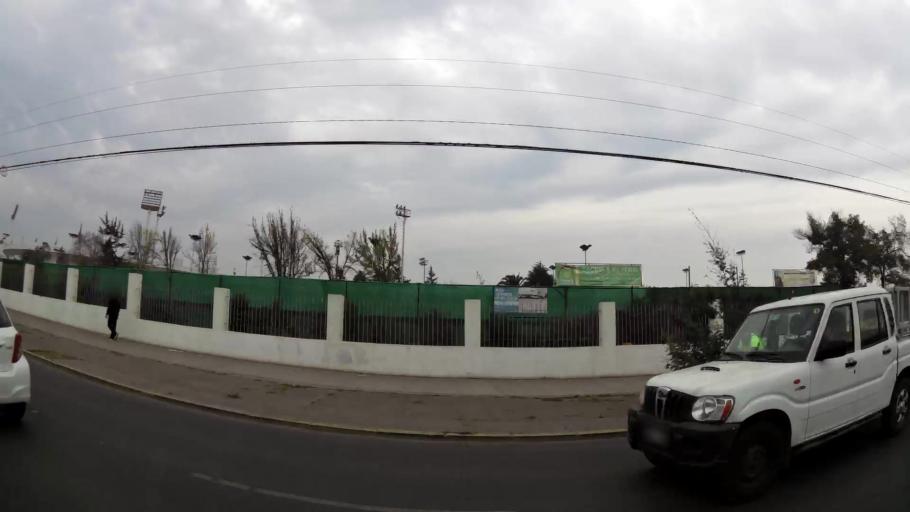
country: CL
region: Santiago Metropolitan
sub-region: Provincia de Santiago
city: Villa Presidente Frei, Nunoa, Santiago, Chile
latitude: -33.4620
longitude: -70.6124
